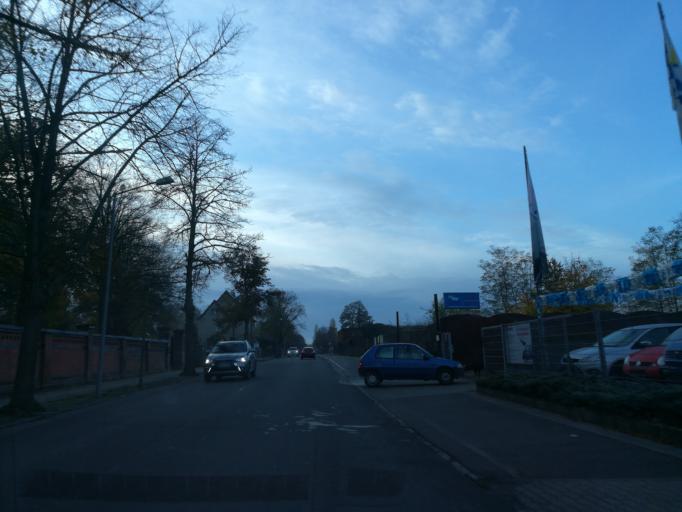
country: DE
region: Saxony-Anhalt
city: Haldensleben I
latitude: 52.2844
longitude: 11.4220
